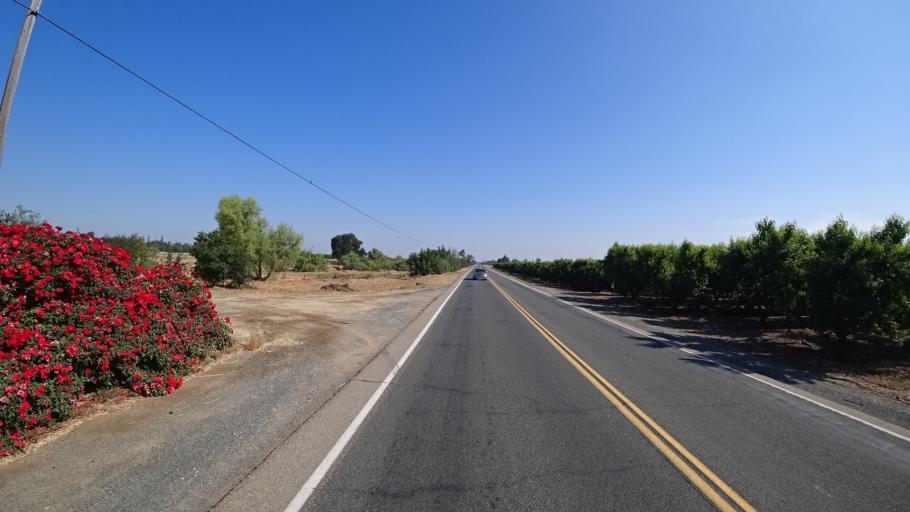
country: US
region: California
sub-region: Fresno County
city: Kingsburg
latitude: 36.4445
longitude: -119.5647
